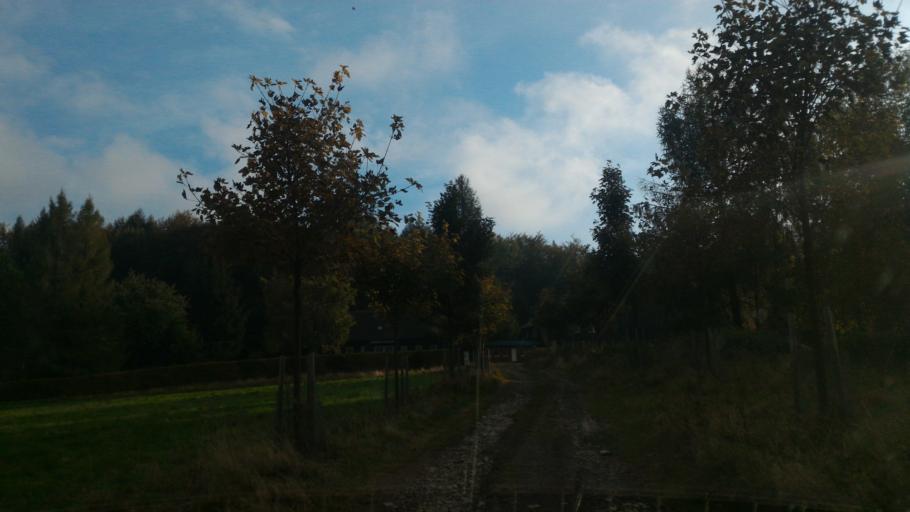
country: CZ
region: Ustecky
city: Dolni Podluzi
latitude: 50.8647
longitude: 14.5657
